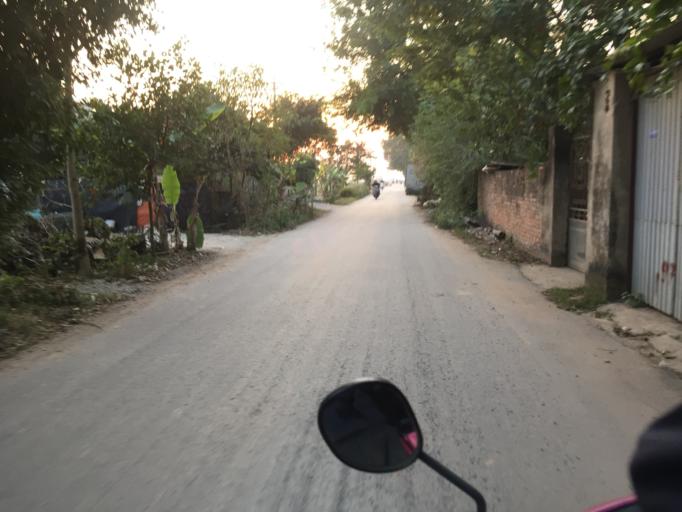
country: VN
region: Ha Noi
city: Chuc Son
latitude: 20.8926
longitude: 105.7226
